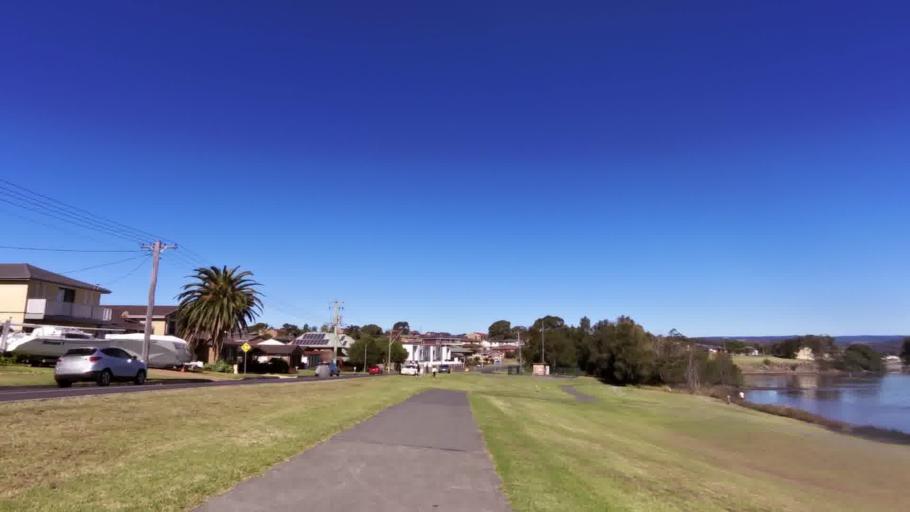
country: AU
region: New South Wales
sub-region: Shellharbour
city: Lake Illawarra
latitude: -34.5500
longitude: 150.8369
